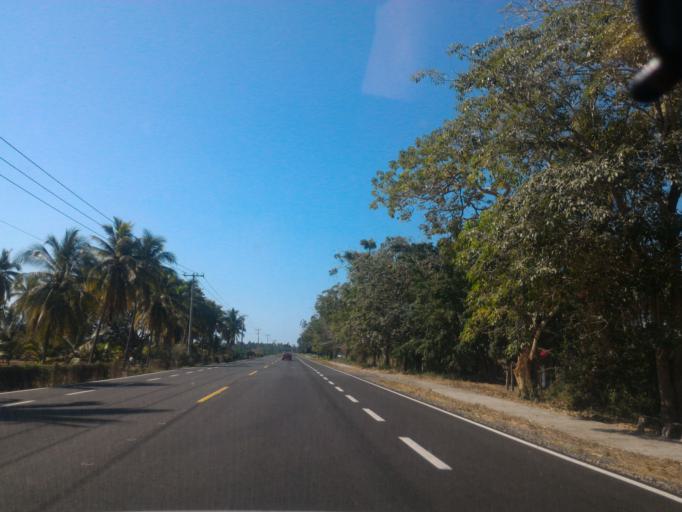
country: MX
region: Colima
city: Tecoman
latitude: 18.8817
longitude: -103.9248
